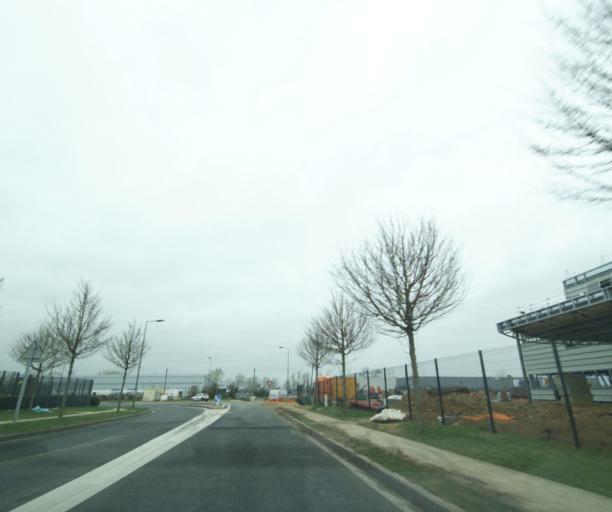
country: FR
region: Ile-de-France
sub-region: Departement du Val-d'Oise
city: Vaureal
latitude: 49.0561
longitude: 2.0327
